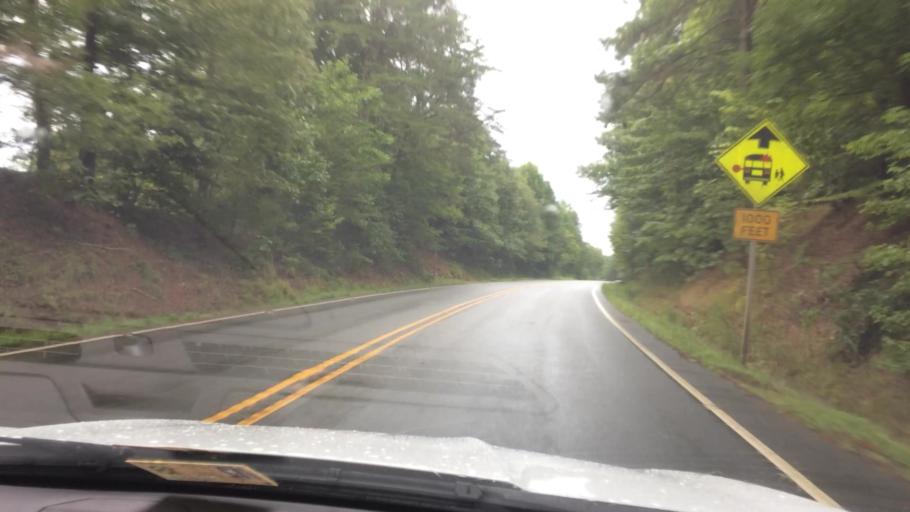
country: US
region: Virginia
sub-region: King William County
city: West Point
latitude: 37.5570
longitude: -76.7413
